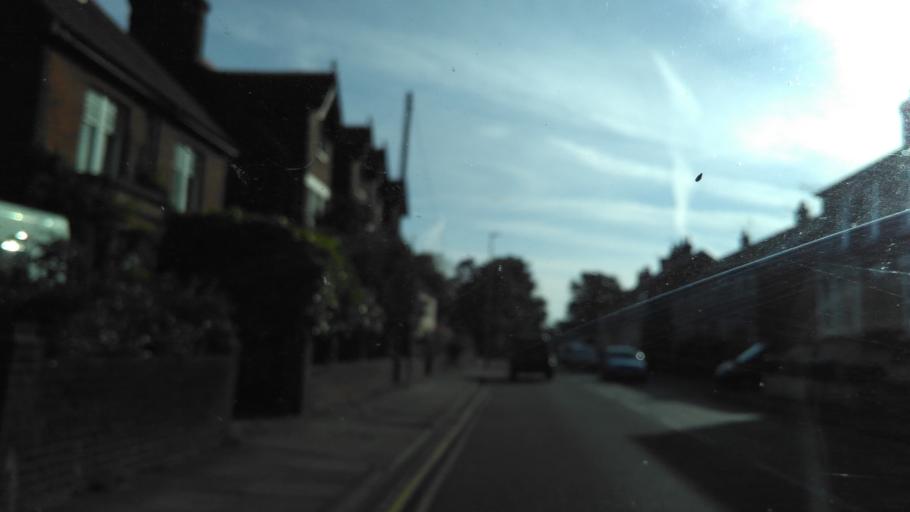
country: GB
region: England
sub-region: Kent
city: Canterbury
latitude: 51.2710
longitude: 1.0658
